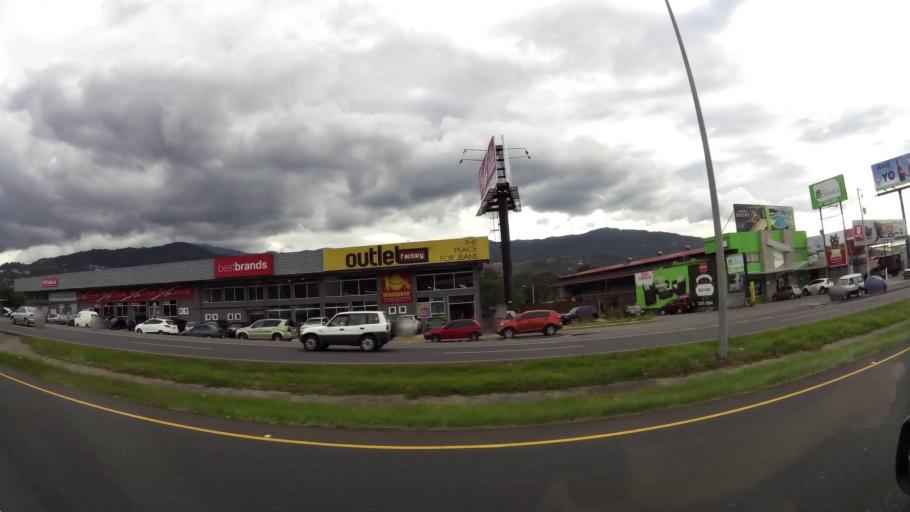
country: CR
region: San Jose
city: Santa Ana
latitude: 9.9468
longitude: -84.1838
